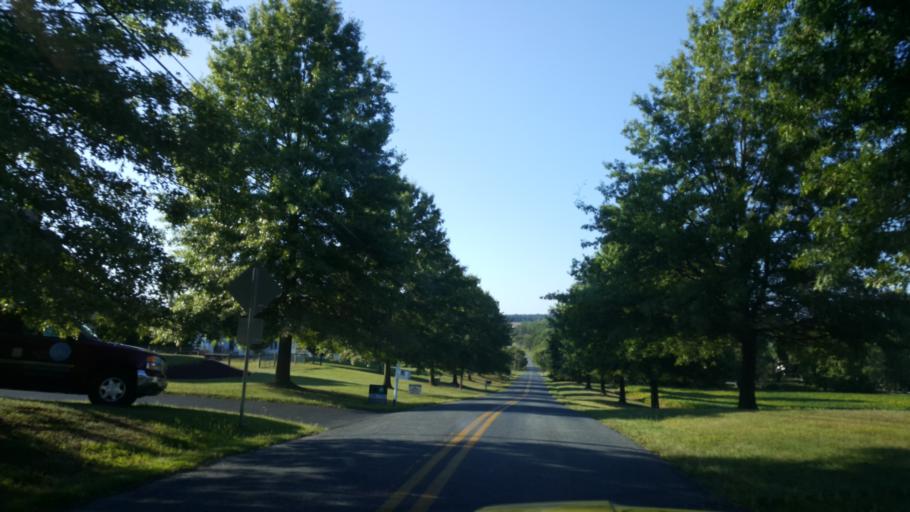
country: US
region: Pennsylvania
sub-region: Lancaster County
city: Rheems
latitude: 40.1674
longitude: -76.5432
